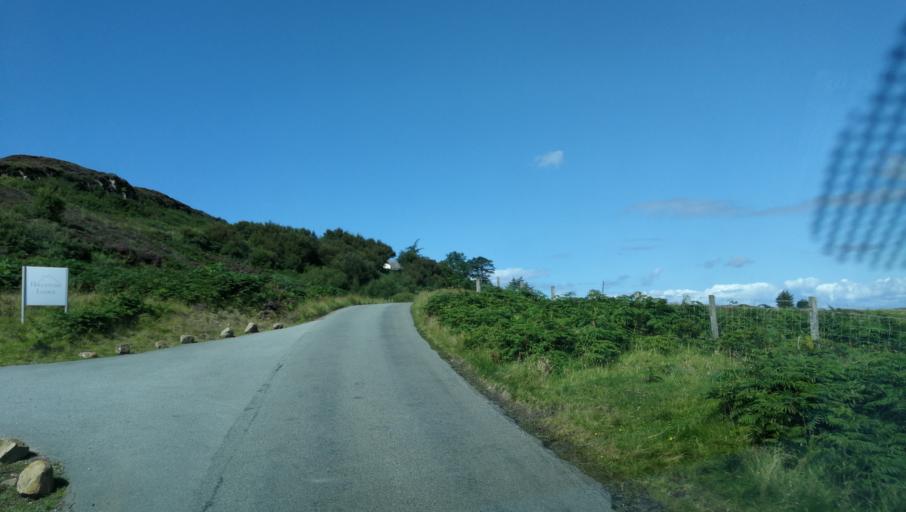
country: GB
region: Scotland
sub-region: Highland
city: Isle of Skye
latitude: 57.4501
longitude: -6.6543
